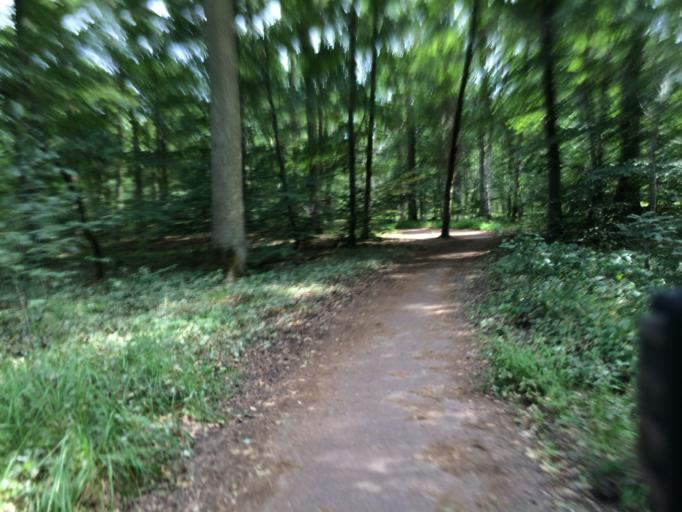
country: FR
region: Ile-de-France
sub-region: Departement de l'Essonne
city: Brunoy
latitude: 48.6663
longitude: 2.4899
